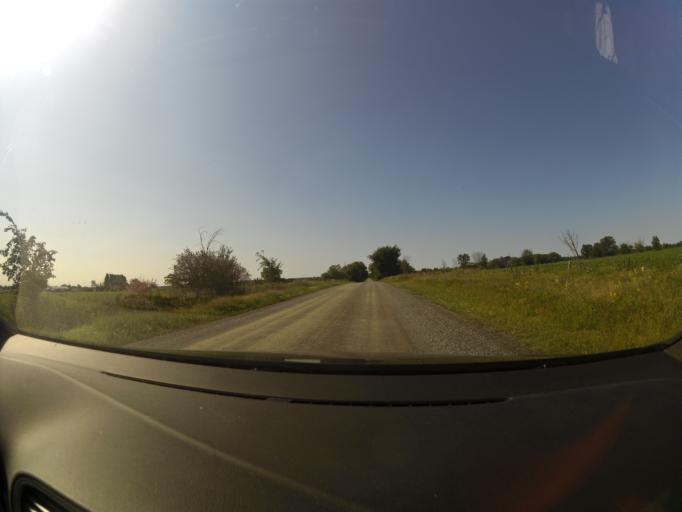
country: CA
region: Ontario
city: Arnprior
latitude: 45.3667
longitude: -76.2884
